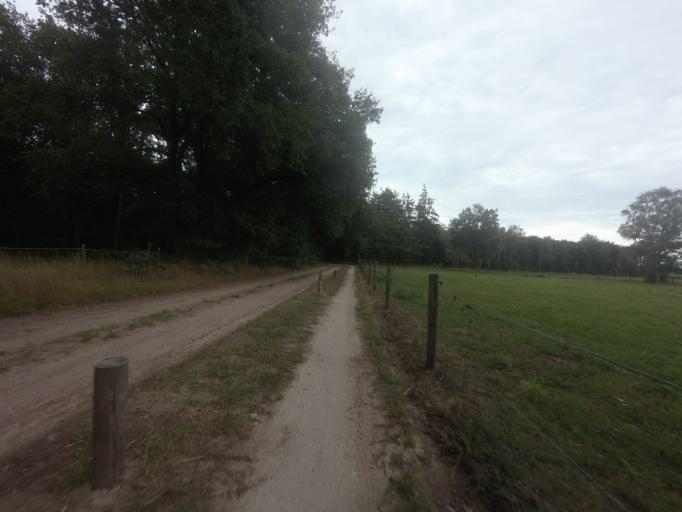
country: NL
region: Overijssel
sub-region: Gemeente Raalte
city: Raalte
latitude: 52.3165
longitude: 6.2921
